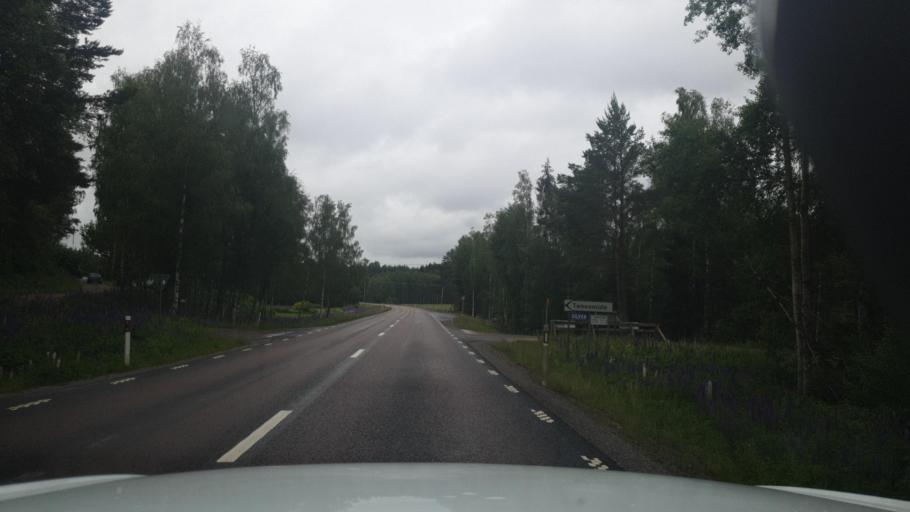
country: SE
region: Vaermland
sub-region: Arvika Kommun
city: Arvika
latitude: 59.5584
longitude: 12.7241
